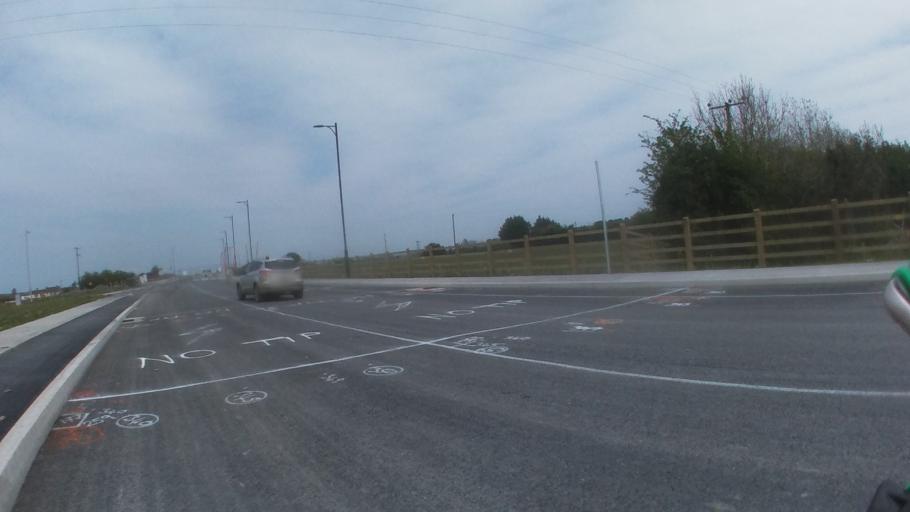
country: IE
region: Leinster
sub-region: Kilkenny
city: Kilkenny
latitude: 52.6419
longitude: -7.2683
